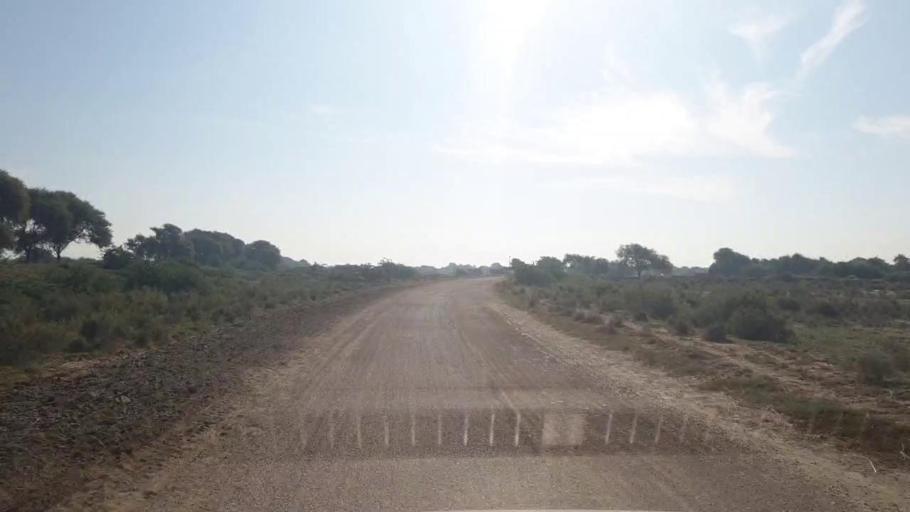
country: PK
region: Sindh
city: Rajo Khanani
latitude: 24.9737
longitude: 68.7855
